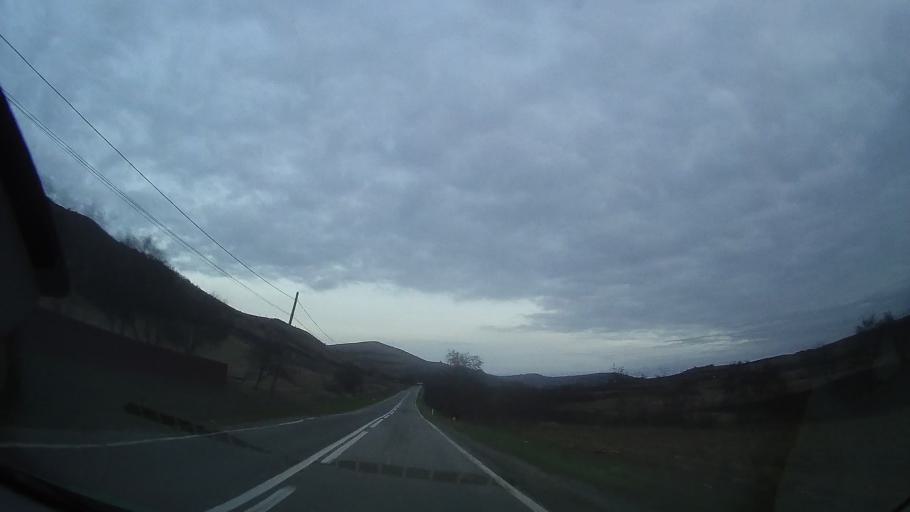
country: RO
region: Cluj
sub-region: Comuna Caianu
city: Caianu
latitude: 46.8004
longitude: 23.9413
